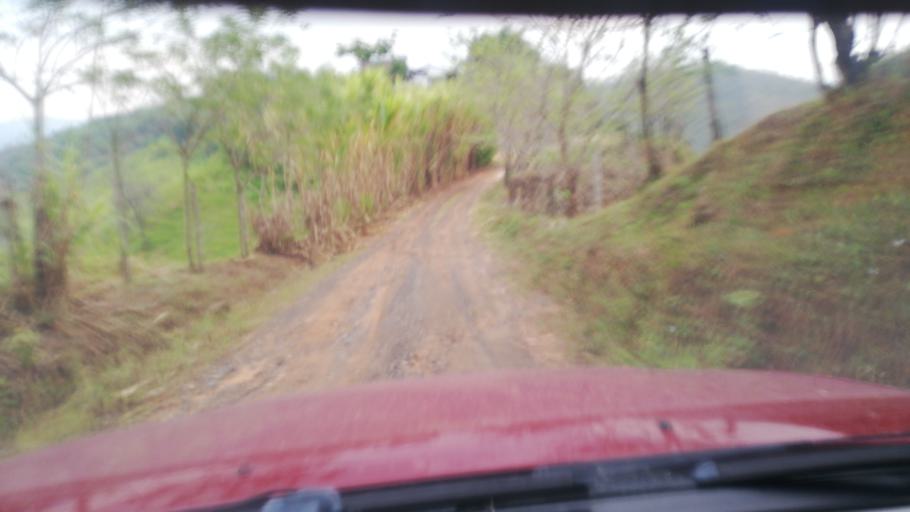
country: CO
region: Risaralda
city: Balboa
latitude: 4.8886
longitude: -75.9625
